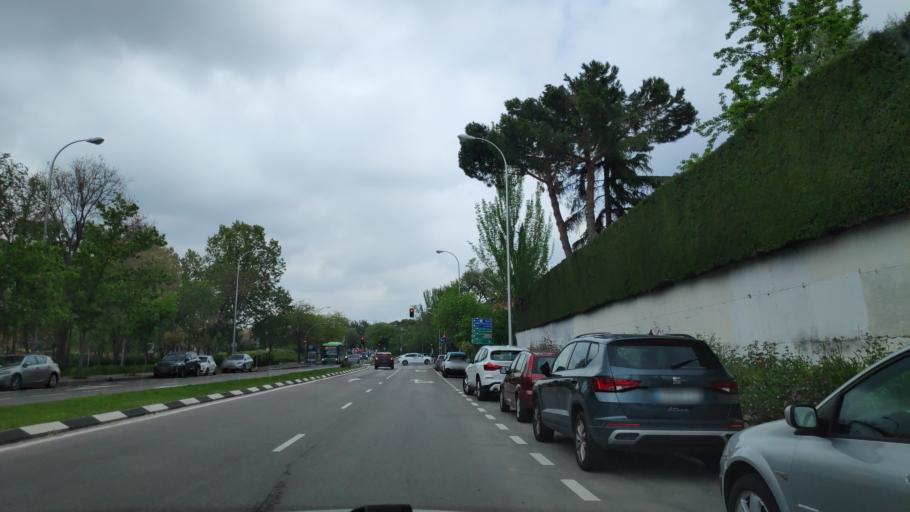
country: ES
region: Madrid
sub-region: Provincia de Madrid
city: Pozuelo de Alarcon
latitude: 40.4584
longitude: -3.7873
